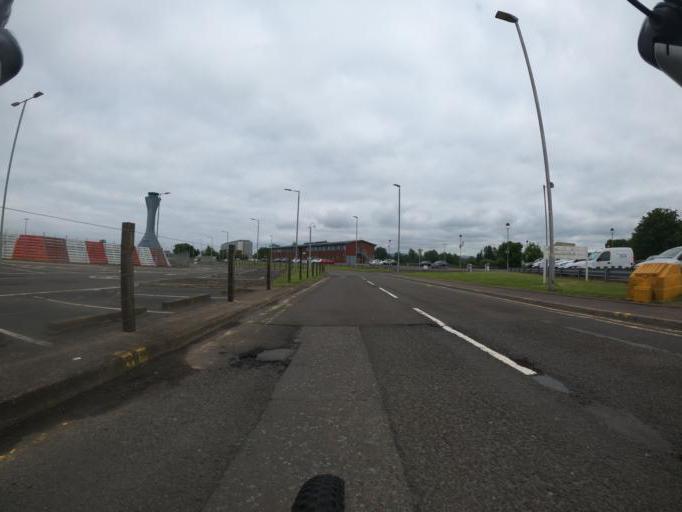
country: GB
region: Scotland
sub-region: Edinburgh
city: Ratho
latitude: 55.9455
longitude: -3.3686
